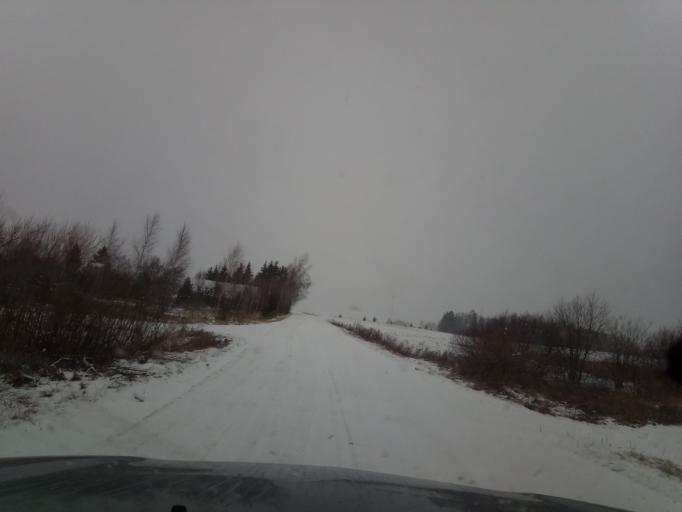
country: LT
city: Ramygala
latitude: 55.5628
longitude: 24.3509
